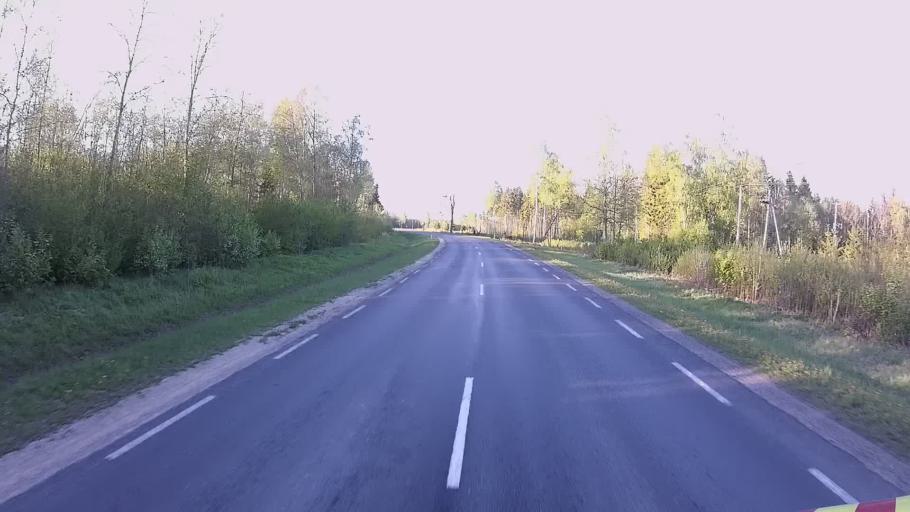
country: EE
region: Viljandimaa
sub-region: Viiratsi vald
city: Viiratsi
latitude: 58.4584
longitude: 25.7487
